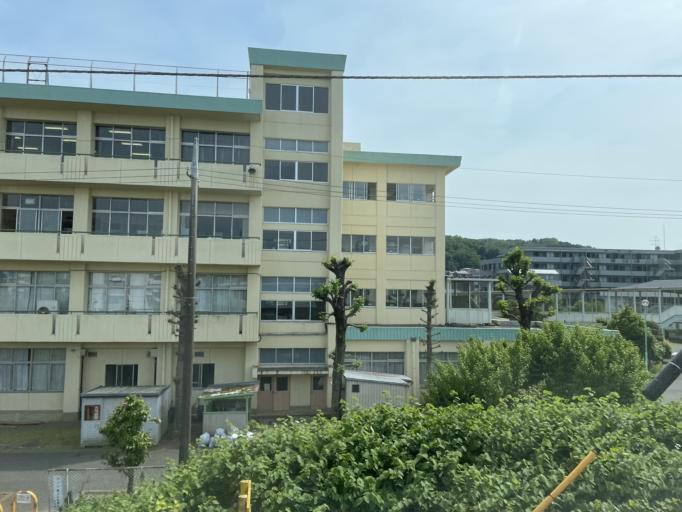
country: JP
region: Saitama
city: Hanno
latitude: 35.8382
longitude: 139.3518
